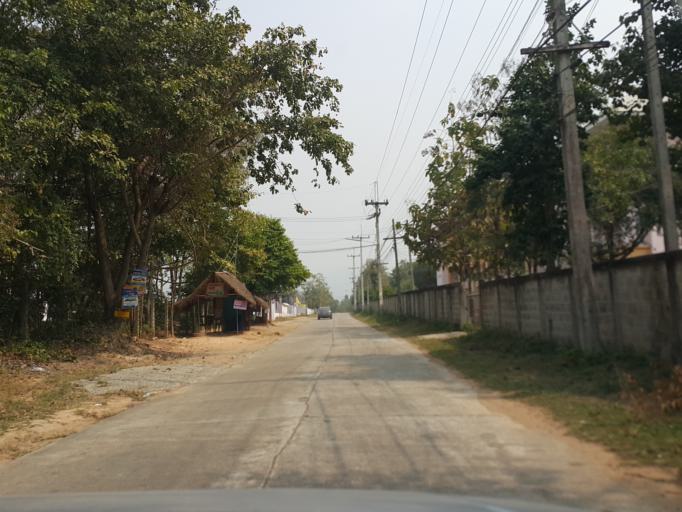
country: TH
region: Lampang
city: Thoen
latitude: 17.6365
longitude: 99.2425
